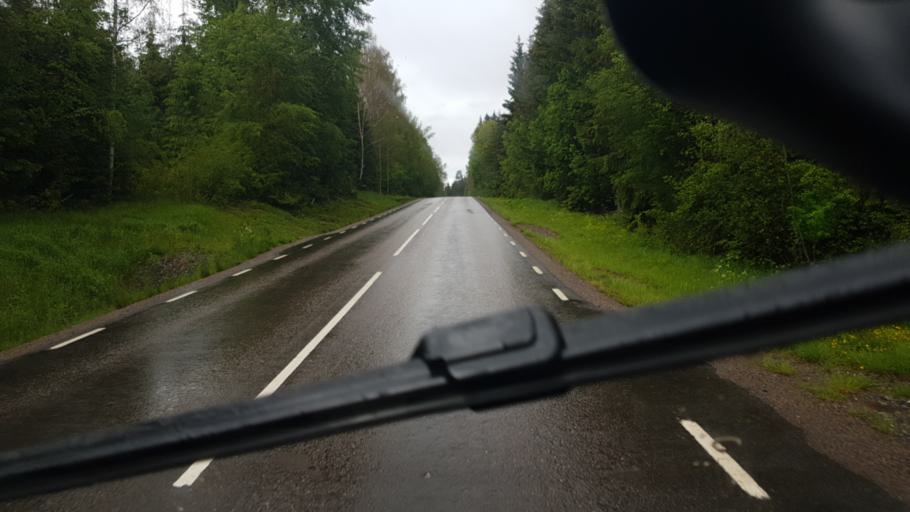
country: SE
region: Vaermland
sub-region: Eda Kommun
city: Amotfors
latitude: 59.7260
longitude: 12.4232
